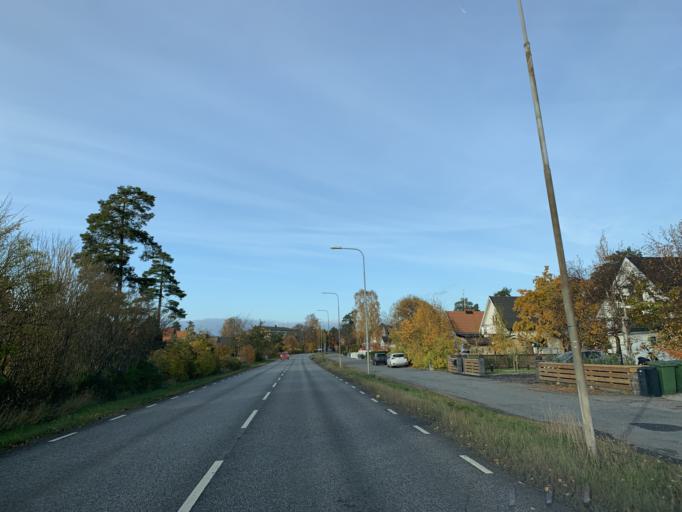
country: SE
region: Stockholm
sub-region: Haninge Kommun
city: Haninge
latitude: 59.1818
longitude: 18.1809
